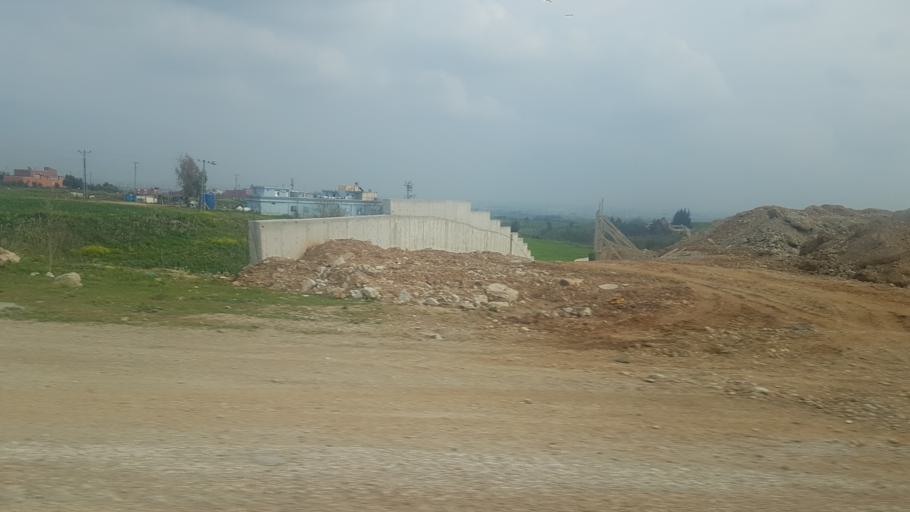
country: TR
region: Adana
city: Seyhan
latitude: 37.0445
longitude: 35.1884
